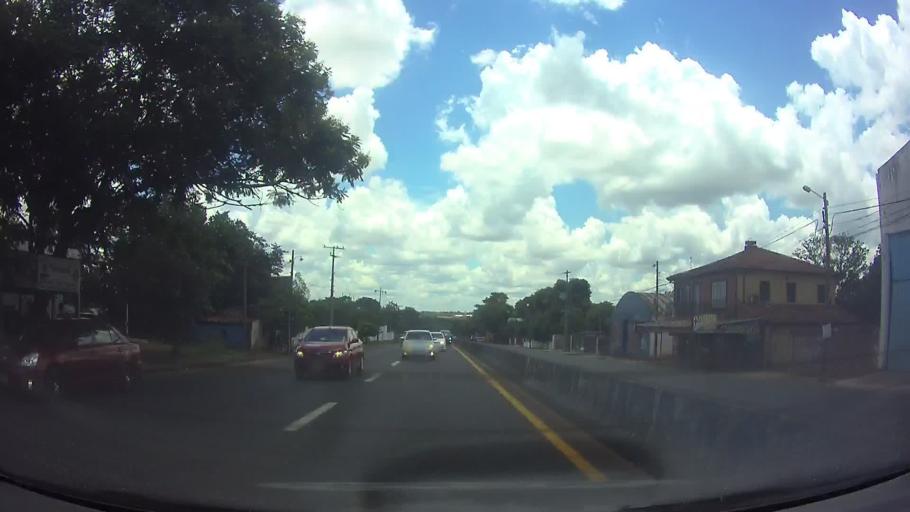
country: PY
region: Central
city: Capiata
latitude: -25.3782
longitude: -57.3932
